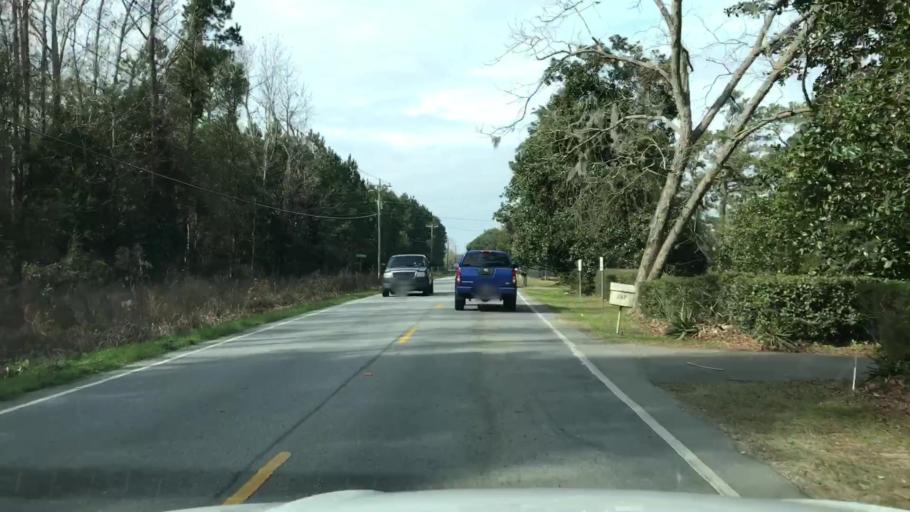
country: US
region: South Carolina
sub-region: Charleston County
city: Shell Point
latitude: 32.7762
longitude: -80.0900
